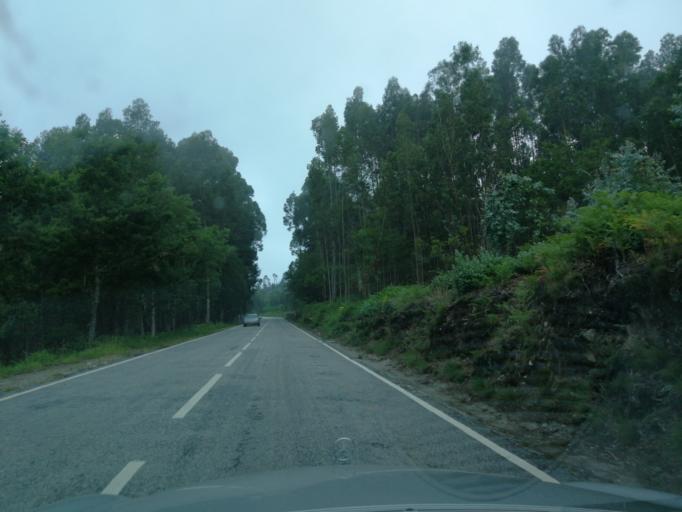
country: PT
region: Braga
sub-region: Braga
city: Braga
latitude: 41.5229
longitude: -8.3815
